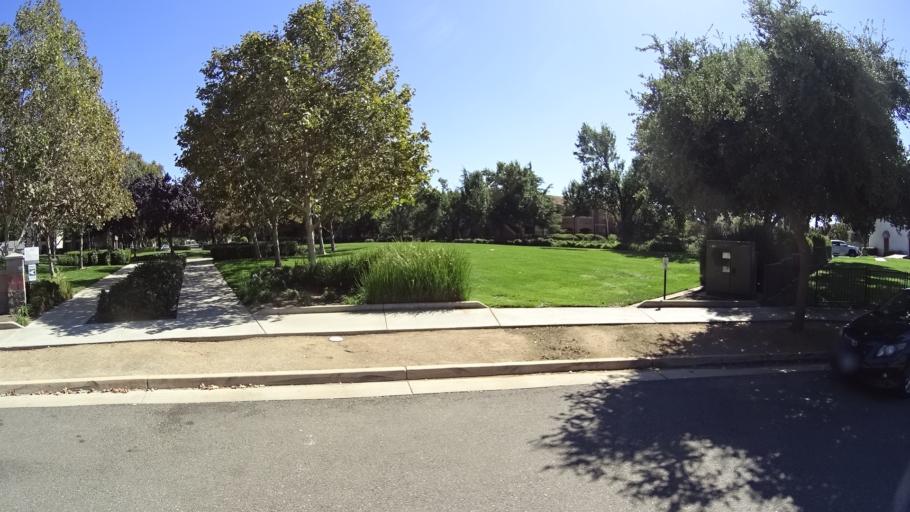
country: US
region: California
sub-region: Sacramento County
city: Laguna
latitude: 38.4254
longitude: -121.4679
